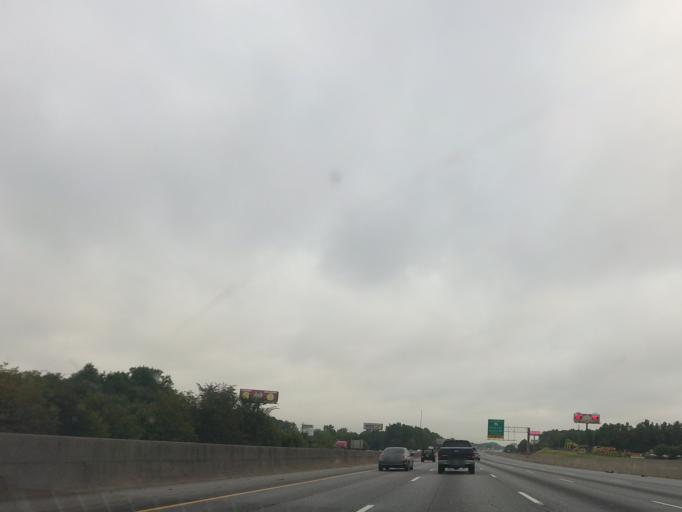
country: US
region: Georgia
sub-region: Clayton County
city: Forest Park
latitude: 33.5966
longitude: -84.3887
